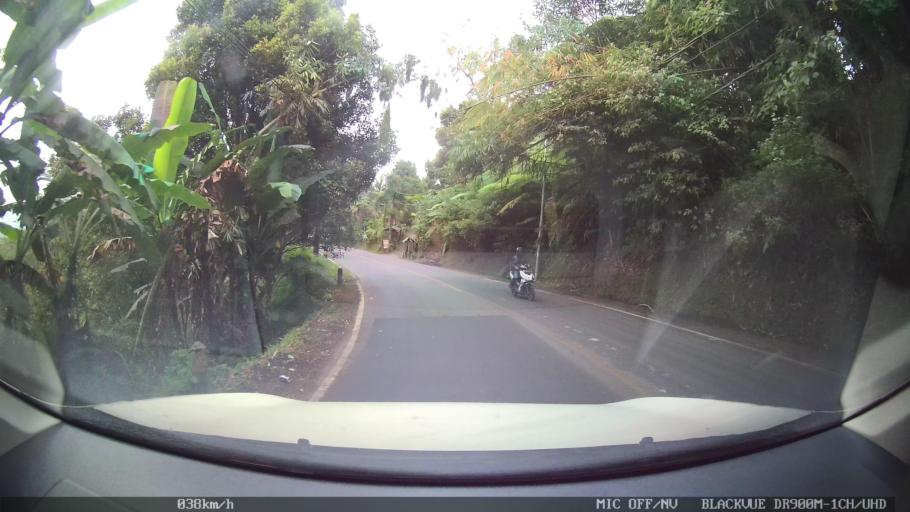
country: ID
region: Bali
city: Banjar Ambengan
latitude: -8.2155
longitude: 115.1429
